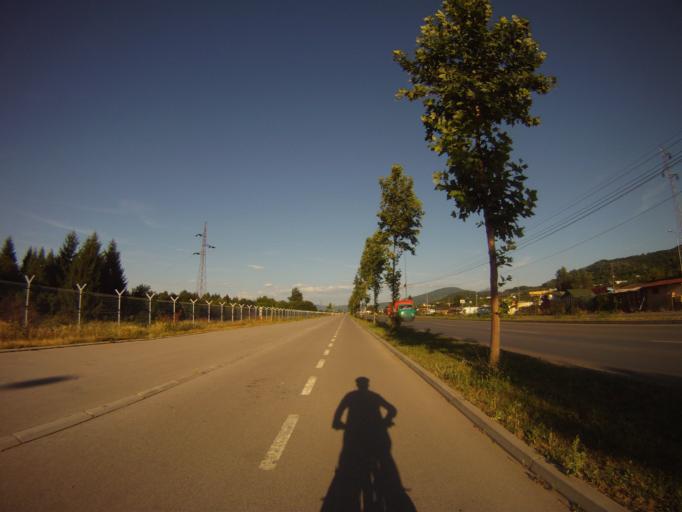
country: RS
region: Central Serbia
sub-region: Nisavski Okrug
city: Nis
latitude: 43.3099
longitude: 21.9384
